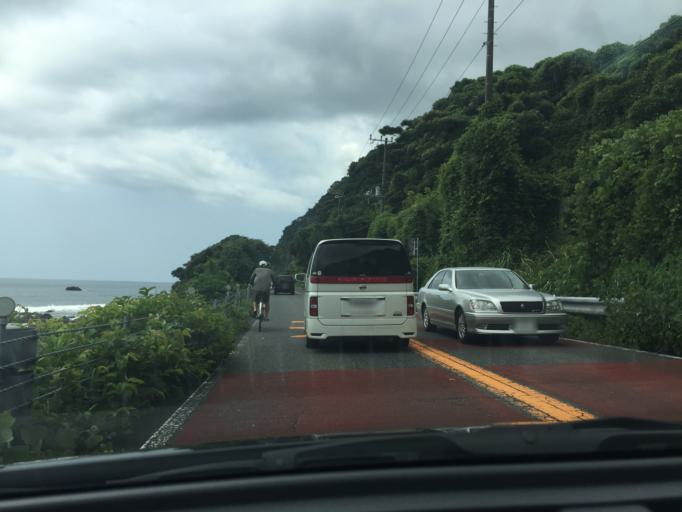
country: JP
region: Shizuoka
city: Ito
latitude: 34.8535
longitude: 139.0824
